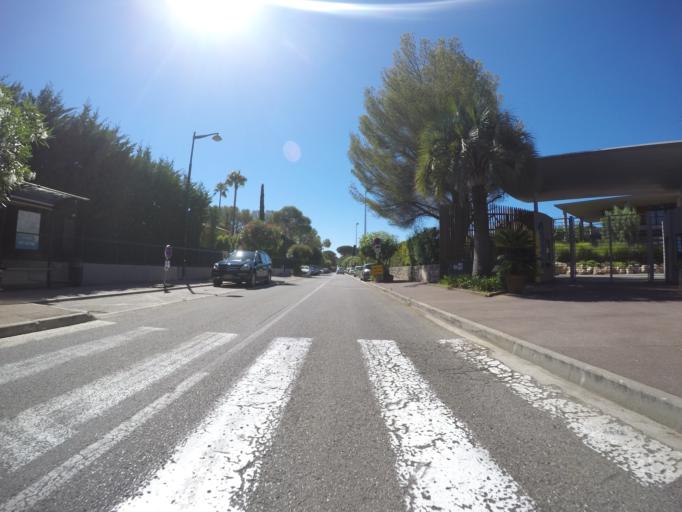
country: FR
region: Provence-Alpes-Cote d'Azur
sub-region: Departement des Alpes-Maritimes
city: Saint-Jean-Cap-Ferrat
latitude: 43.6890
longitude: 7.3291
